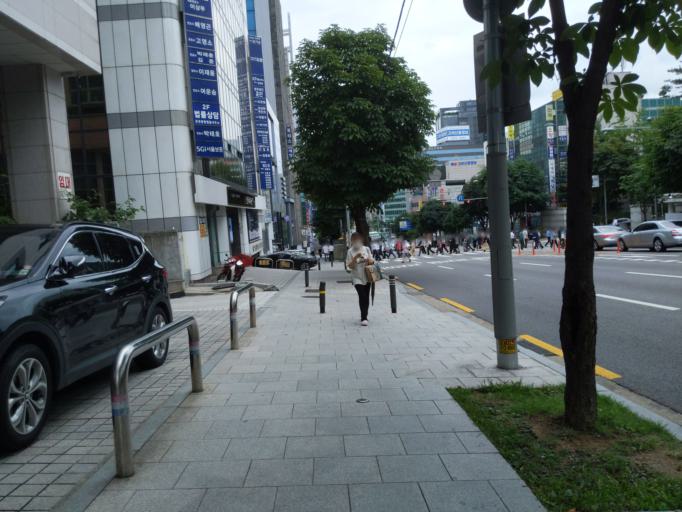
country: KR
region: Seoul
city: Seoul
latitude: 37.4962
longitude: 127.0132
